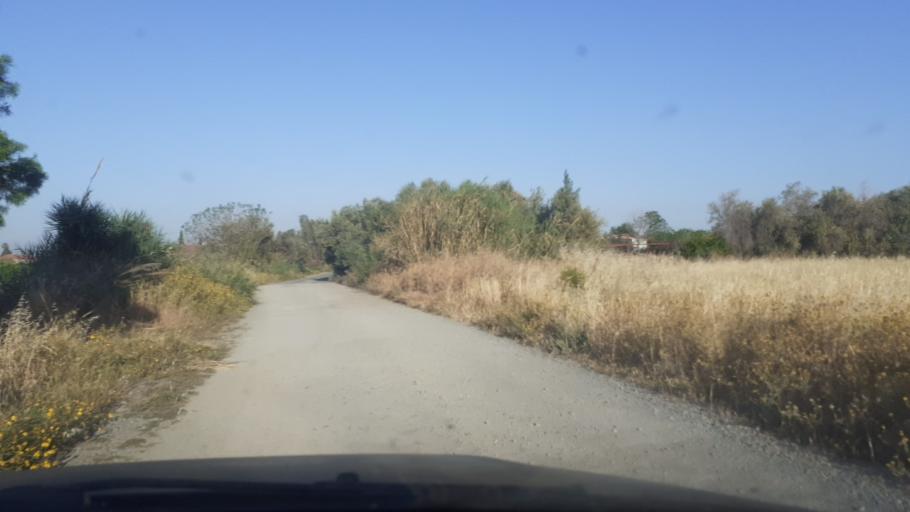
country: CY
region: Larnaka
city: Kolossi
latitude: 34.6693
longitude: 32.9395
